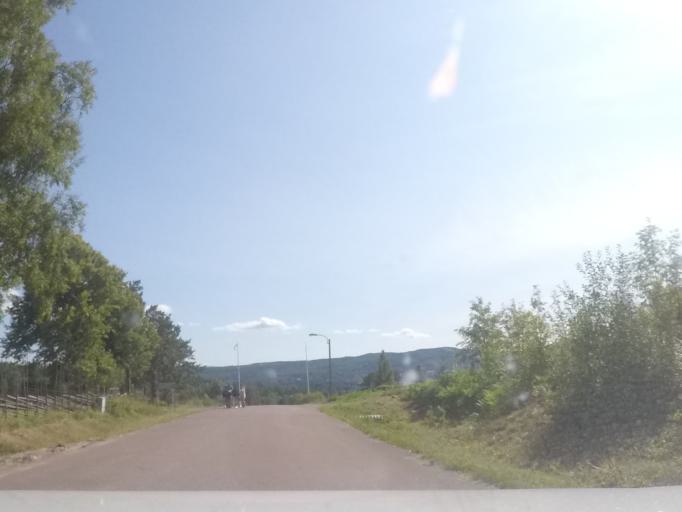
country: SE
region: Dalarna
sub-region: Leksand Municipality
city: Siljansnas
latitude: 60.7860
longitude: 14.8609
